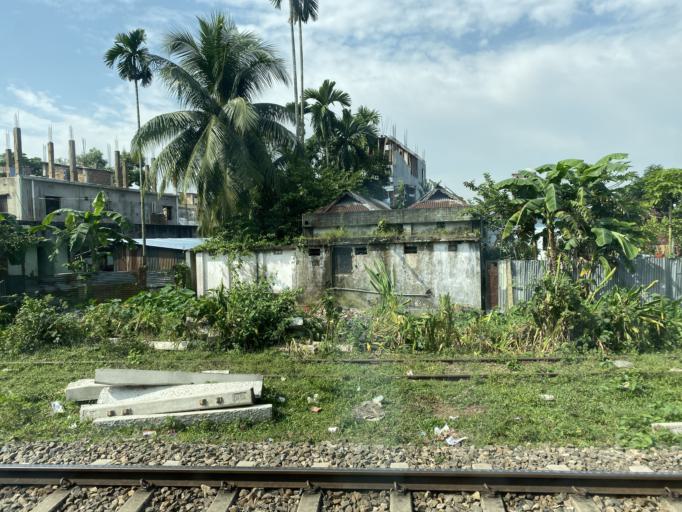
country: BD
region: Sylhet
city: Habiganj
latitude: 24.1787
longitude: 91.3571
